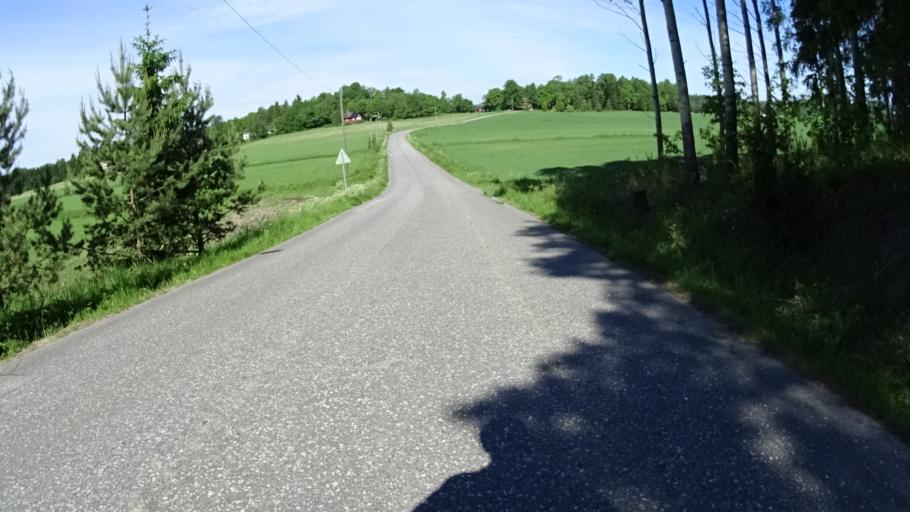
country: FI
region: Uusimaa
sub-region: Helsinki
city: Kilo
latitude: 60.2606
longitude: 24.7764
